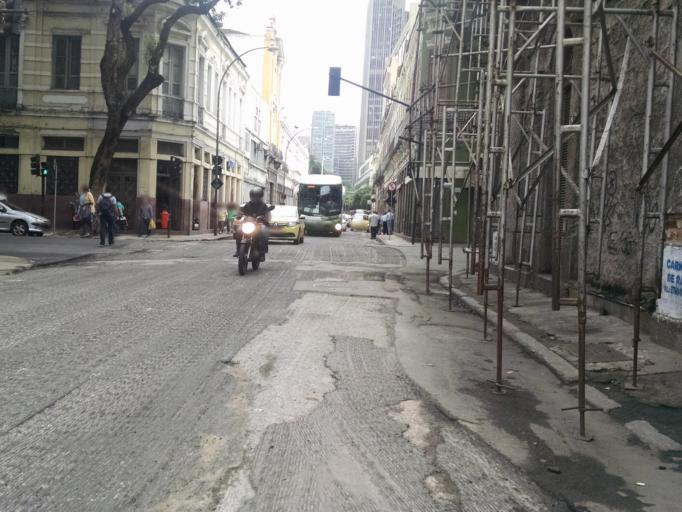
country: BR
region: Rio de Janeiro
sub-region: Rio De Janeiro
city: Rio de Janeiro
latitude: -22.9096
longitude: -43.1847
